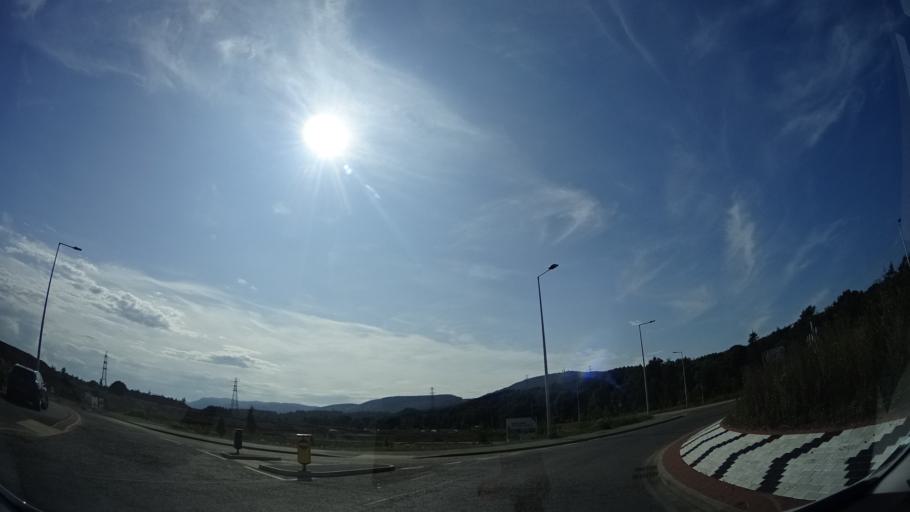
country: GB
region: Scotland
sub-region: Highland
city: Inverness
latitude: 57.4577
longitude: -4.2480
